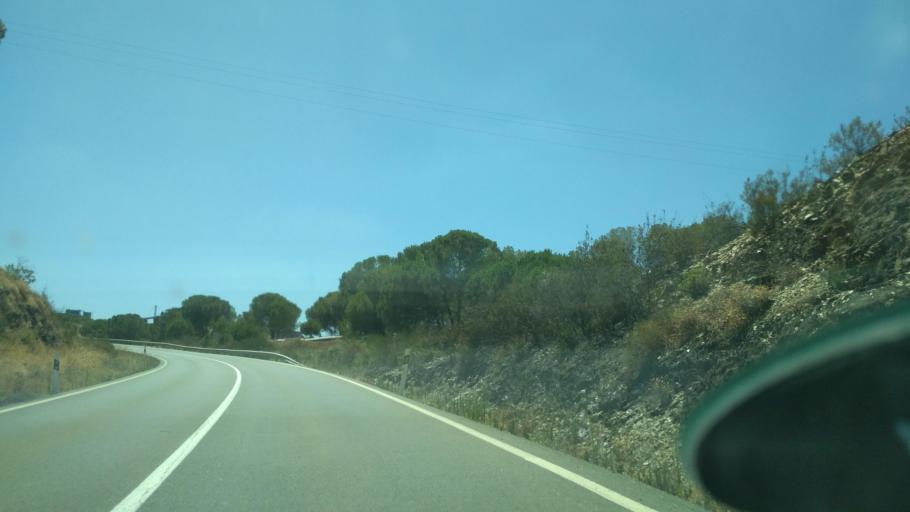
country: ES
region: Andalusia
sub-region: Provincia de Huelva
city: Campofrio
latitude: 37.7260
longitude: -6.5844
